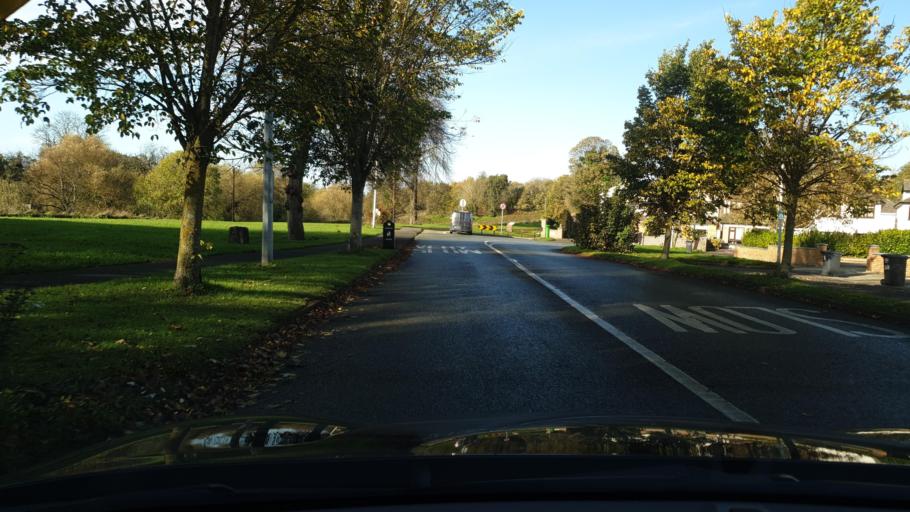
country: IE
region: Leinster
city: Lucan
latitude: 53.3498
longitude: -6.4393
